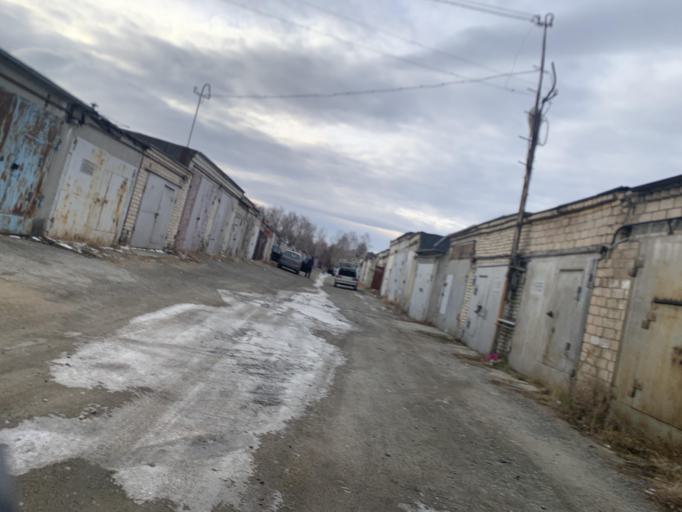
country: RU
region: Chelyabinsk
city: Roshchino
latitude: 55.1882
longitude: 61.2676
